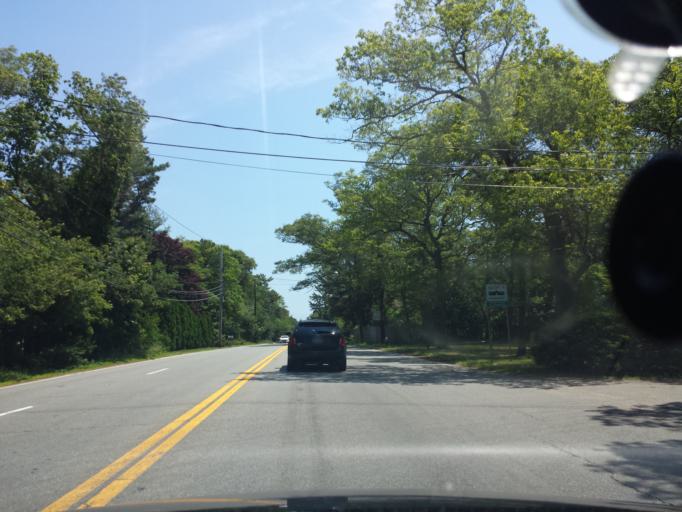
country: US
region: Massachusetts
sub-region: Barnstable County
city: Osterville
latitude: 41.6533
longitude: -70.3909
